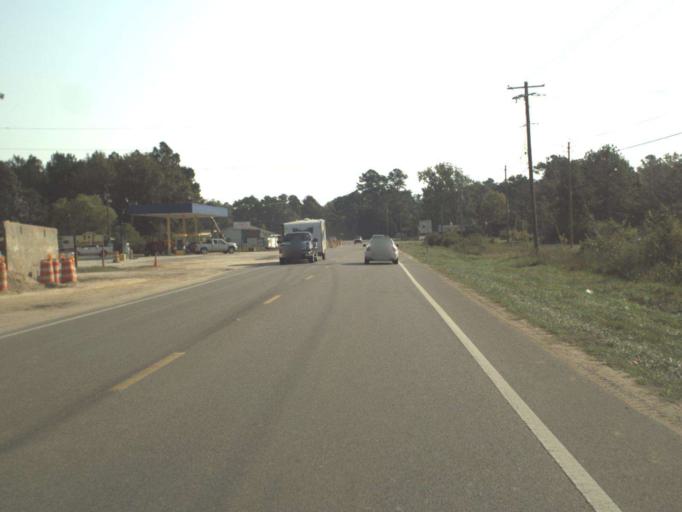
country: US
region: Florida
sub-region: Holmes County
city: Bonifay
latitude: 30.6083
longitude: -85.7194
